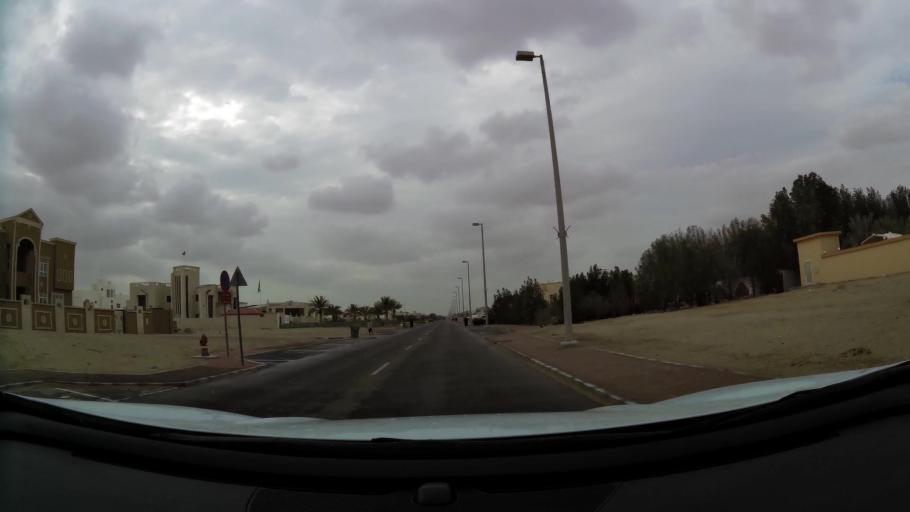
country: AE
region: Abu Dhabi
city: Abu Dhabi
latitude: 24.3510
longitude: 54.6356
